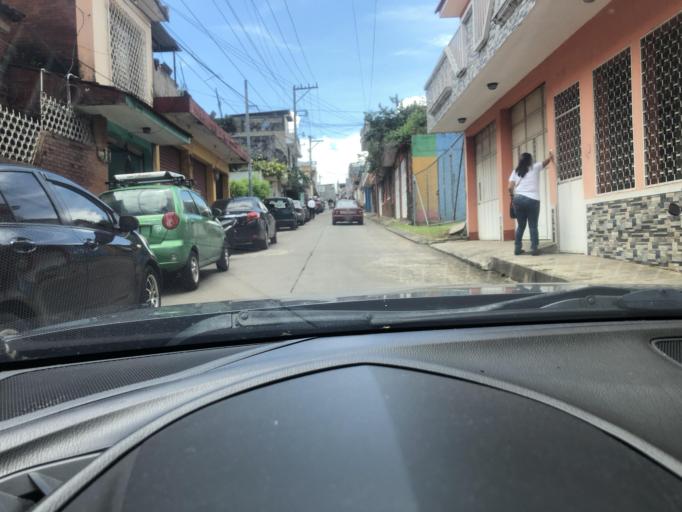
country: GT
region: Quetzaltenango
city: Coatepeque
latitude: 14.7073
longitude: -91.8684
